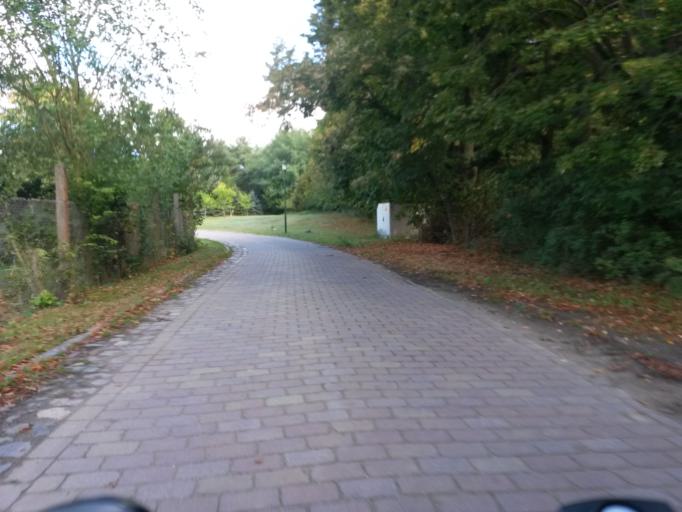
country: DE
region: Brandenburg
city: Templin
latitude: 53.2112
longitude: 13.5164
